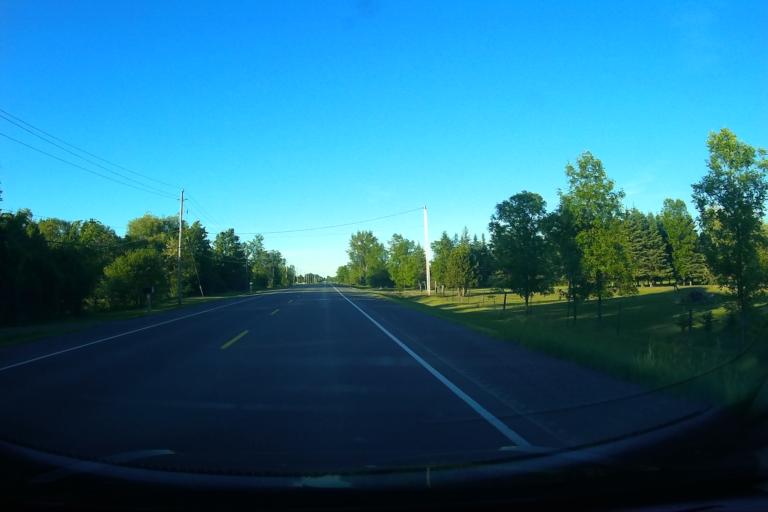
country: CA
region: Ontario
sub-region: Lanark County
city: Smiths Falls
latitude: 44.9695
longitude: -75.7515
